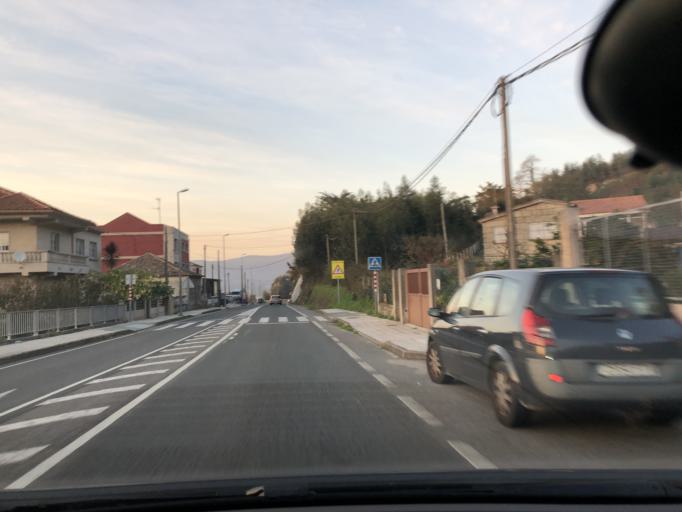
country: ES
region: Galicia
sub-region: Provincia de Pontevedra
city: Marin
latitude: 42.3888
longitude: -8.7119
